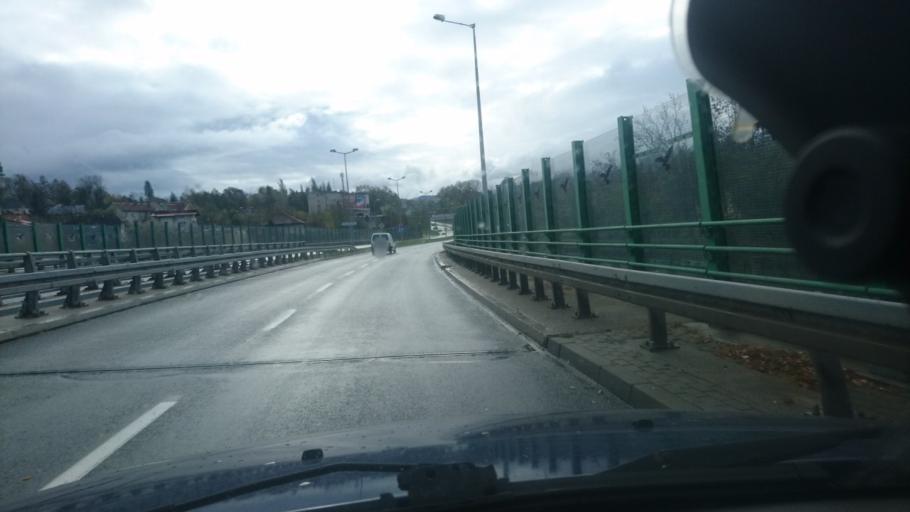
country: PL
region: Silesian Voivodeship
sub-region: Bielsko-Biala
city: Bielsko-Biala
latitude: 49.8258
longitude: 19.0155
